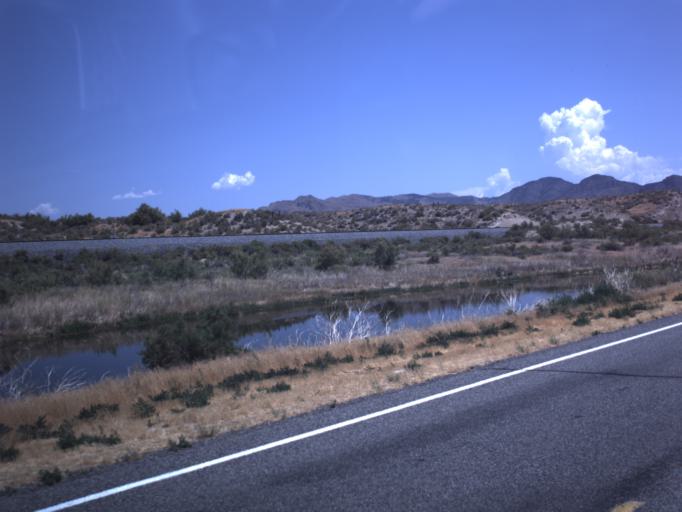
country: US
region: Utah
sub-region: Millard County
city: Delta
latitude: 39.5265
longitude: -112.3588
